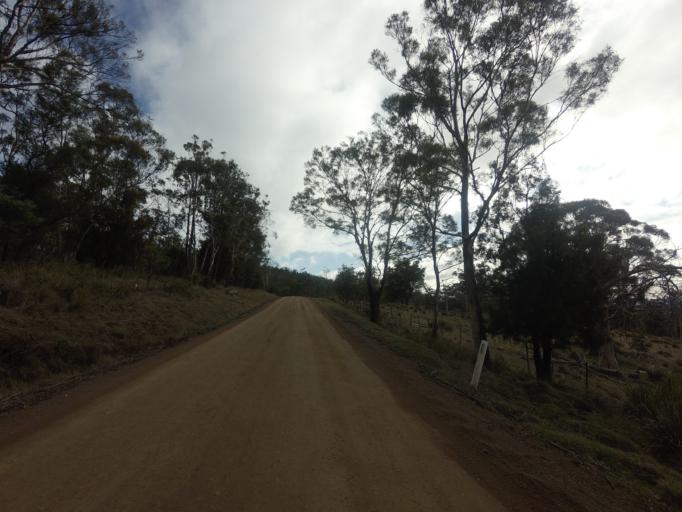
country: AU
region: Tasmania
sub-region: Derwent Valley
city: New Norfolk
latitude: -42.7372
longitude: 146.8696
